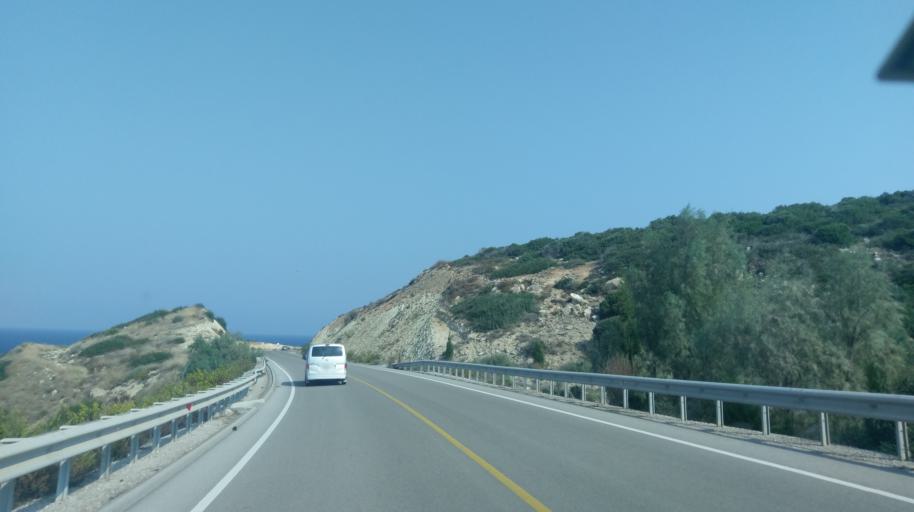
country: CY
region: Ammochostos
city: Leonarisso
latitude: 35.4568
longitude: 34.0097
